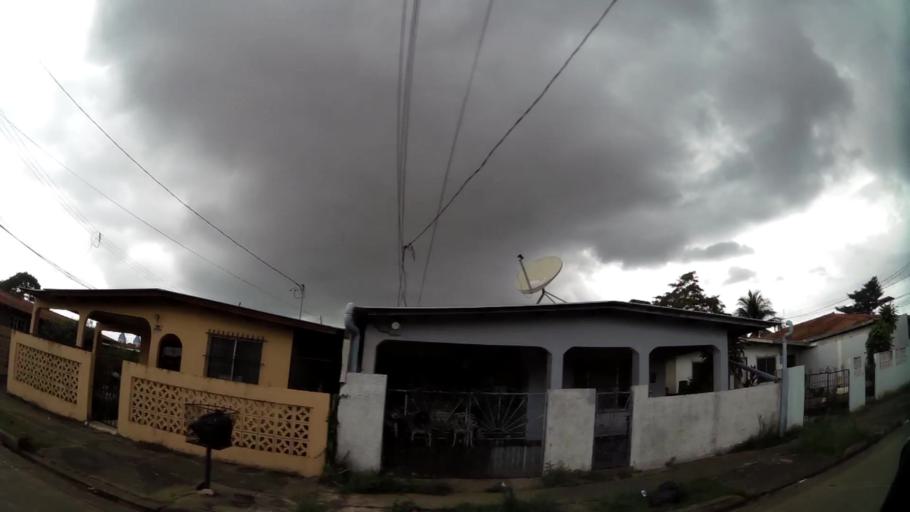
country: PA
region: Panama
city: Tocumen
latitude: 9.0566
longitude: -79.4161
